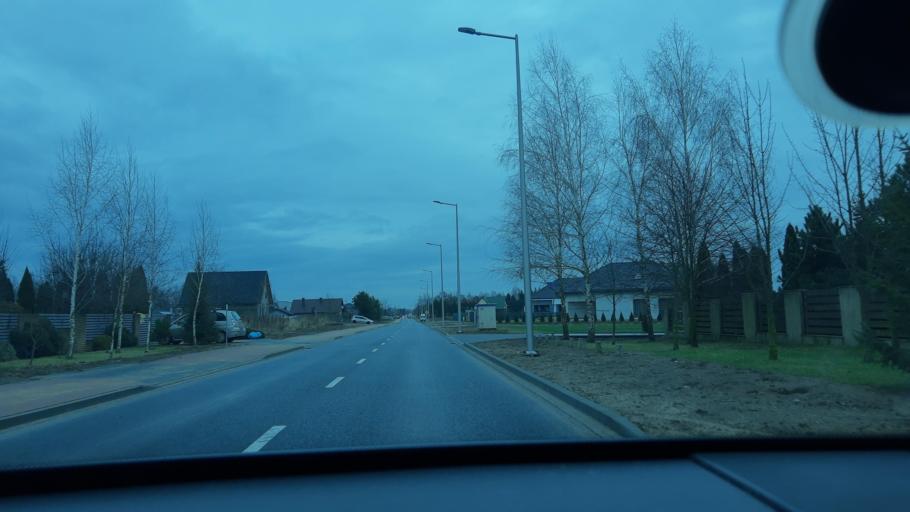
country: PL
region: Lodz Voivodeship
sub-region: Powiat sieradzki
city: Sieradz
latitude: 51.5862
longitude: 18.6879
